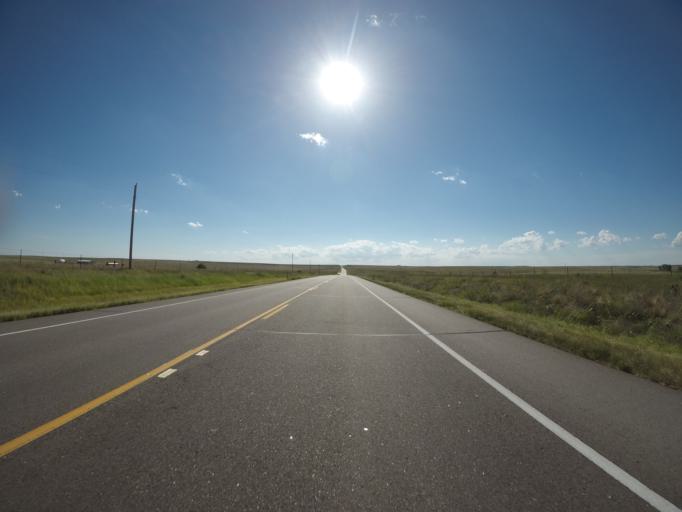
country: US
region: Colorado
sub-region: Logan County
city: Sterling
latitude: 40.6108
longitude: -103.5409
